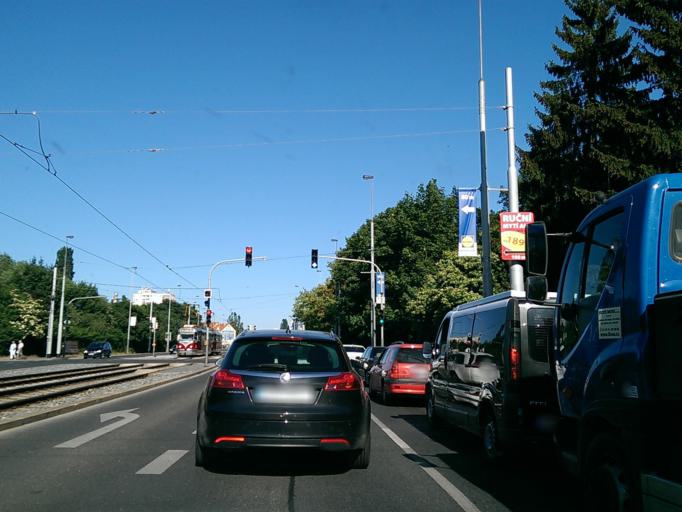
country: CZ
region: Praha
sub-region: Praha 14
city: Hostavice
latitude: 50.0528
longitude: 14.5255
